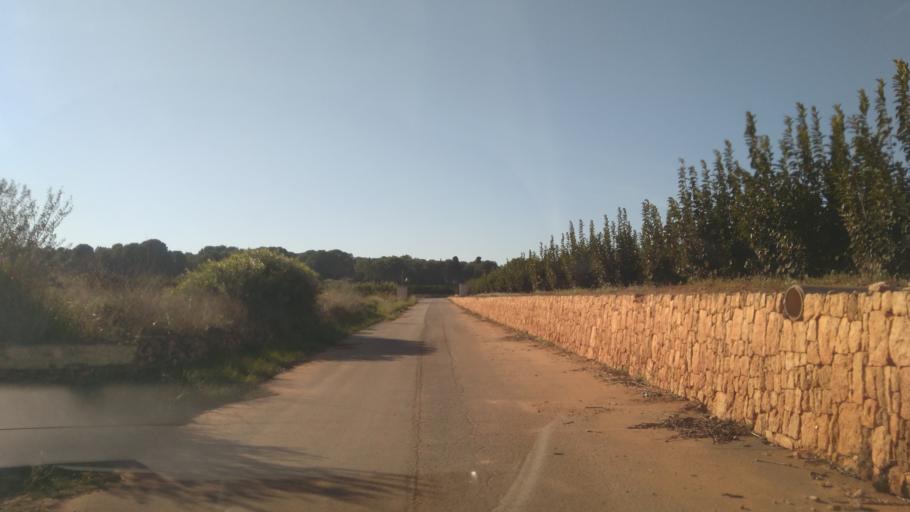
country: ES
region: Valencia
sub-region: Provincia de Valencia
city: Masalaves
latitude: 39.1763
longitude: -0.5544
